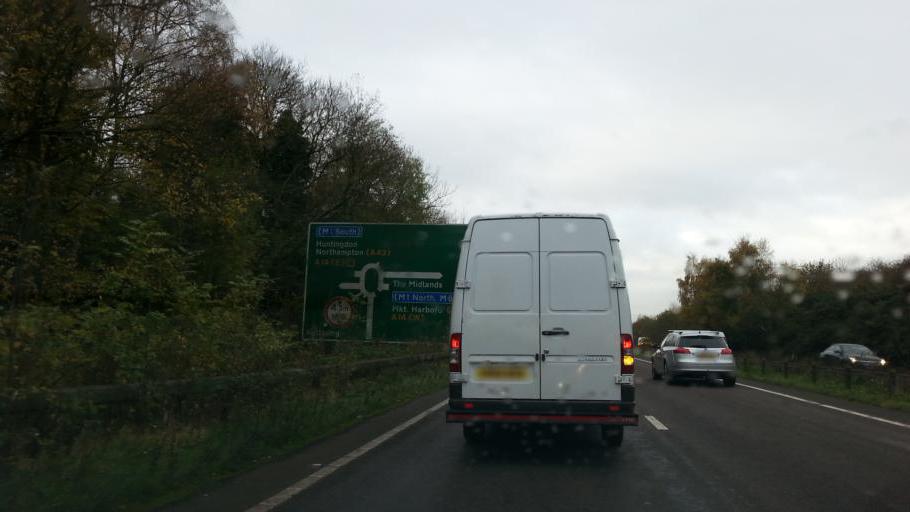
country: GB
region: England
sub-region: Northamptonshire
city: Kettering
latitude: 52.4099
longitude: -0.7498
